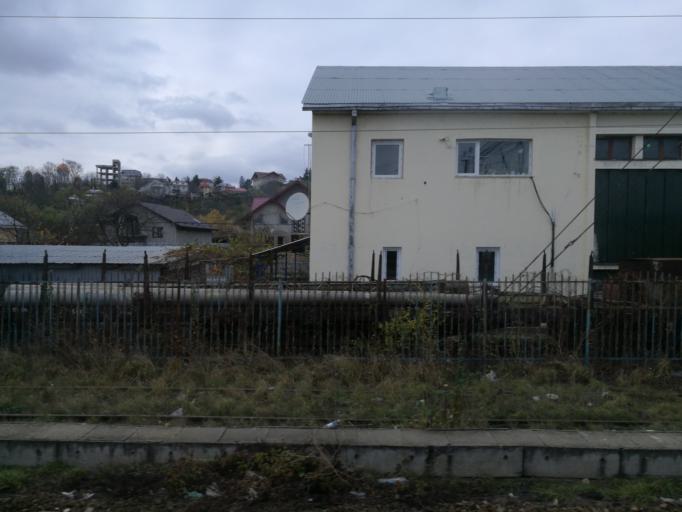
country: RO
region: Iasi
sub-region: Municipiul Pascani
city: Pascani
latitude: 47.2495
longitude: 26.7286
